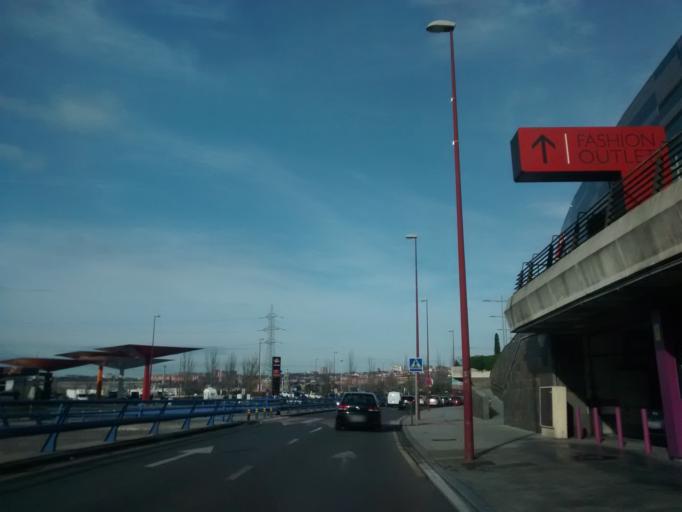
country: ES
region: Basque Country
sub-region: Bizkaia
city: Barakaldo
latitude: 43.2923
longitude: -3.0058
